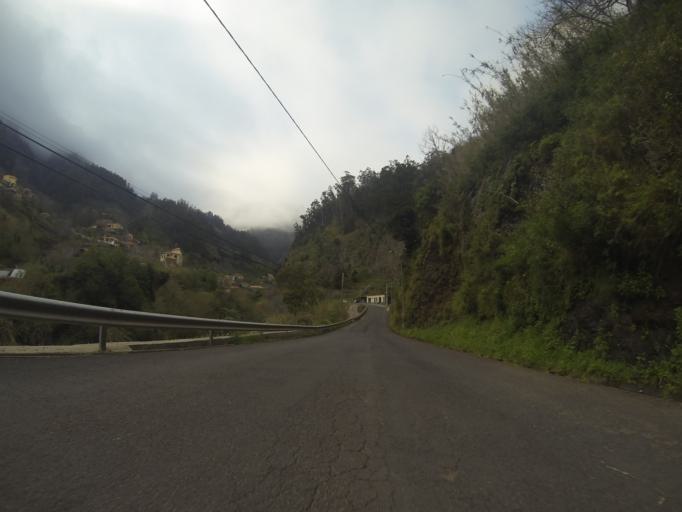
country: PT
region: Madeira
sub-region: Camara de Lobos
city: Curral das Freiras
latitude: 32.7384
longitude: -16.9686
